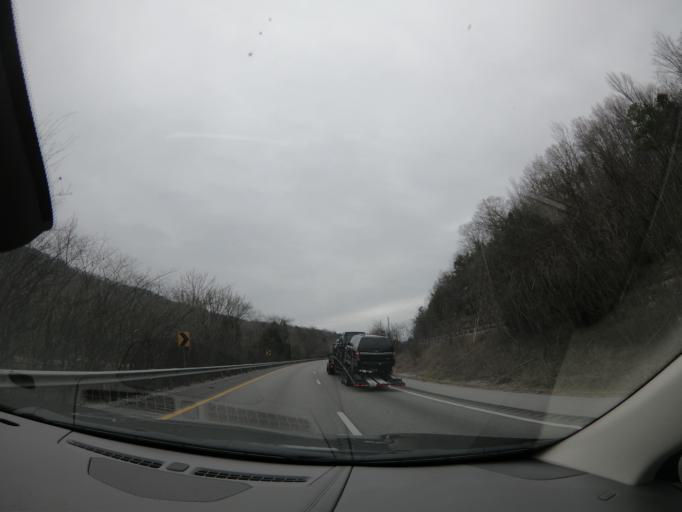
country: US
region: Tennessee
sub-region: Marion County
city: Jasper
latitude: 35.0069
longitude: -85.5256
